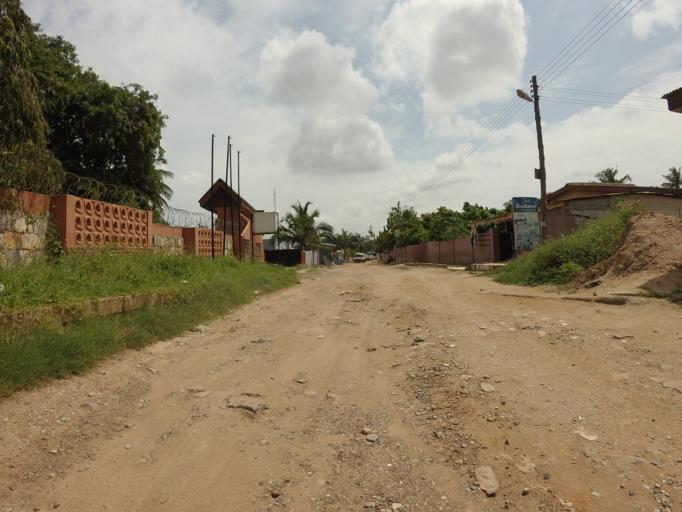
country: GH
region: Greater Accra
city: Dome
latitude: 5.6376
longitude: -0.2365
